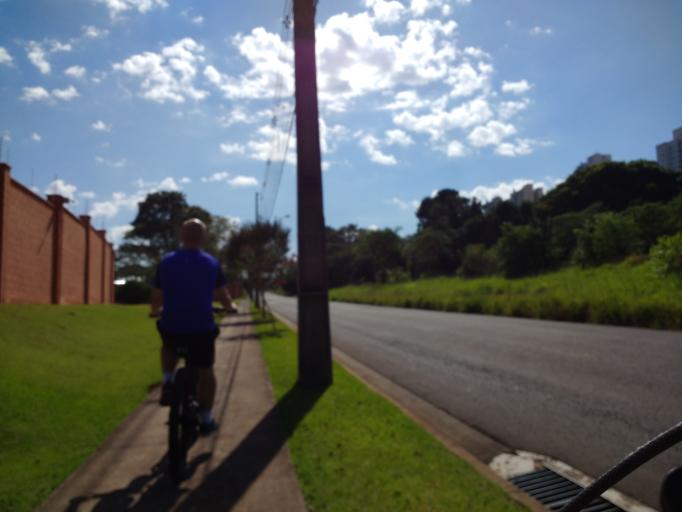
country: BR
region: Parana
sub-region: Londrina
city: Londrina
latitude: -23.3511
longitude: -51.1837
